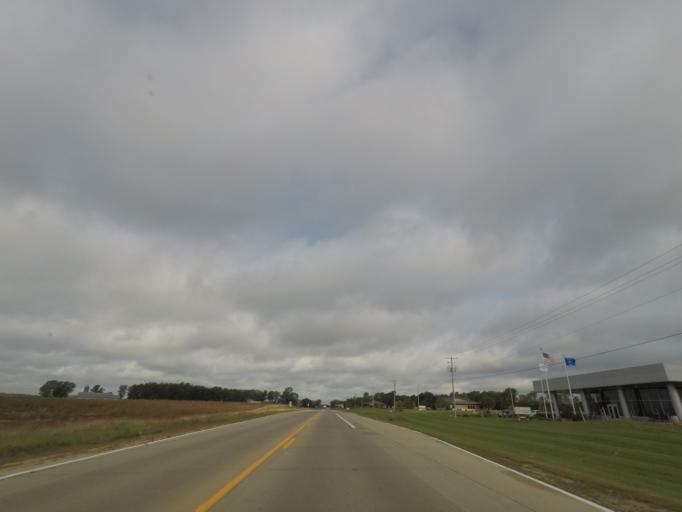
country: US
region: Wisconsin
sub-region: Jefferson County
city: Cambridge
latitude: 43.0121
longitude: -89.0261
